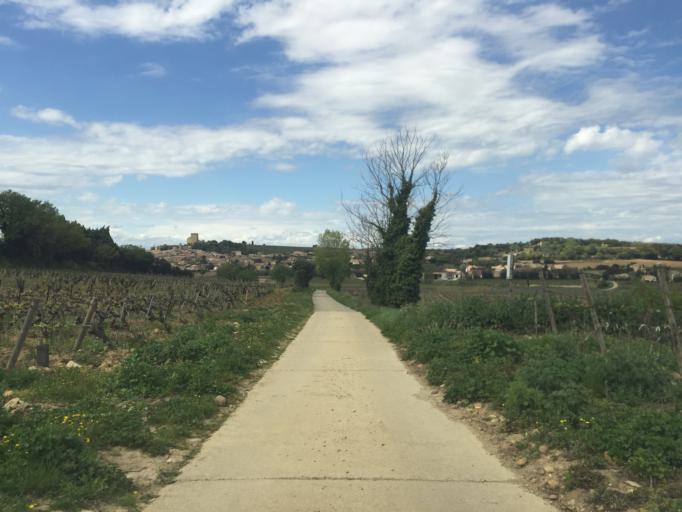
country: FR
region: Provence-Alpes-Cote d'Azur
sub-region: Departement du Vaucluse
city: Chateauneuf-du-Pape
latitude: 44.0582
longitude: 4.8467
